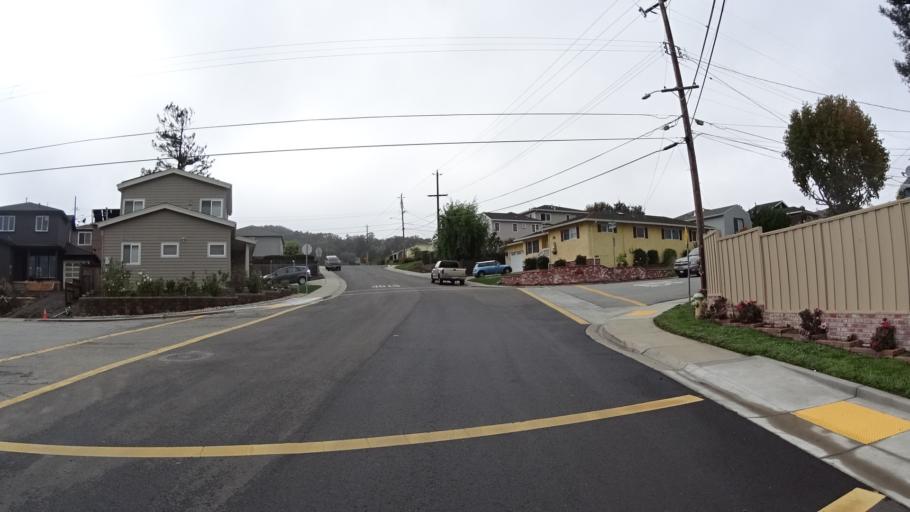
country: US
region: California
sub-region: San Mateo County
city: San Bruno
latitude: 37.6135
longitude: -122.4118
